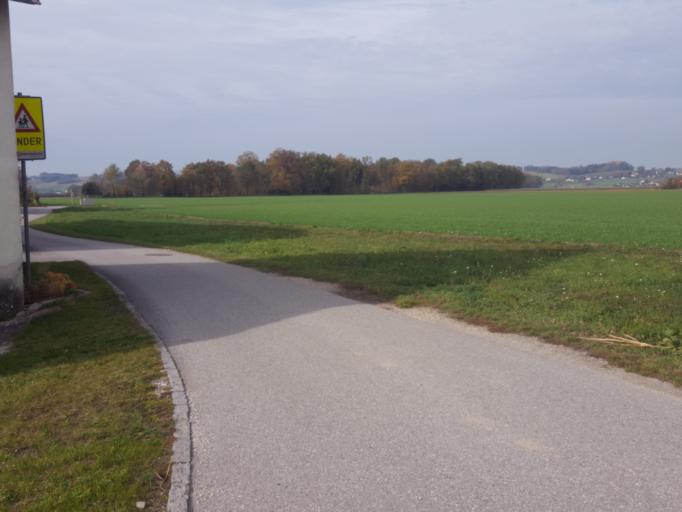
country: AT
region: Upper Austria
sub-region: Politischer Bezirk Perg
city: Perg
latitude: 48.2512
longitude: 14.5689
